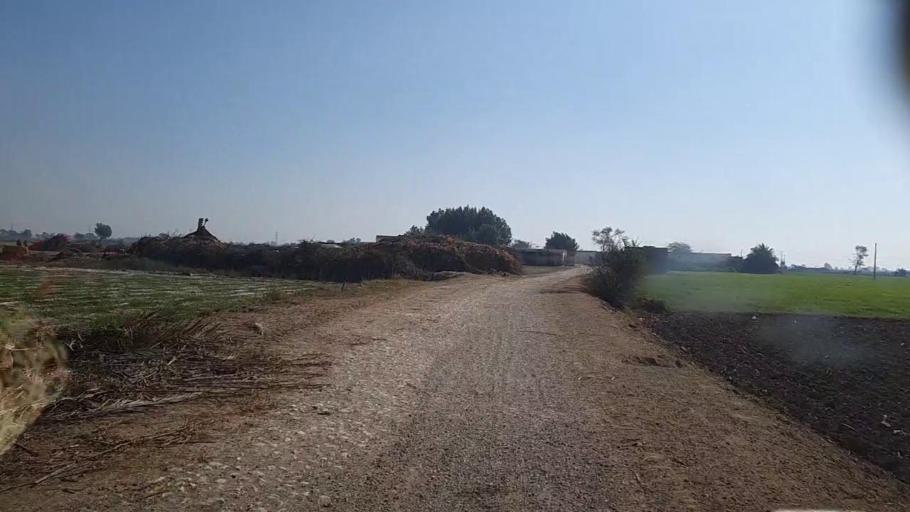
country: PK
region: Sindh
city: Khairpur
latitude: 28.0476
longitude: 69.7806
